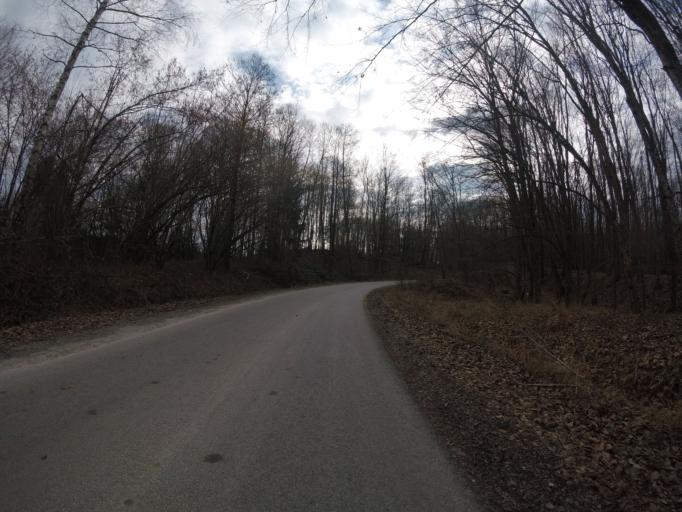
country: HR
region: Sisacko-Moslavacka
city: Glina
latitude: 45.4696
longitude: 16.0325
